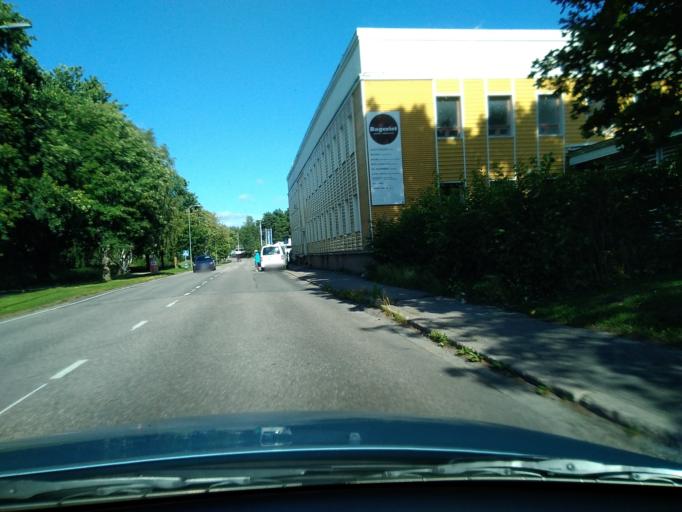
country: FI
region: Uusimaa
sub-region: Raaseporin
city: Ekenaes
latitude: 59.9791
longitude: 23.4460
